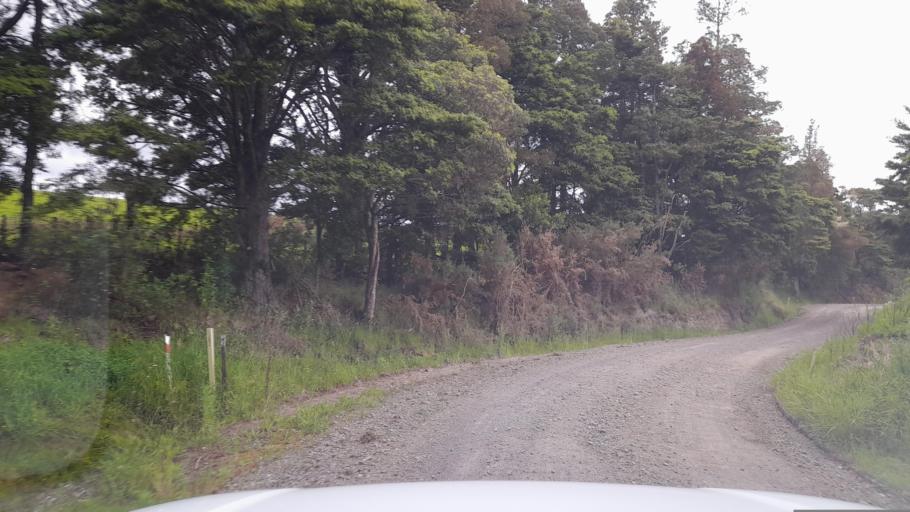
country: NZ
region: Northland
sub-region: Far North District
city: Waimate North
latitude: -35.3958
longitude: 173.7848
